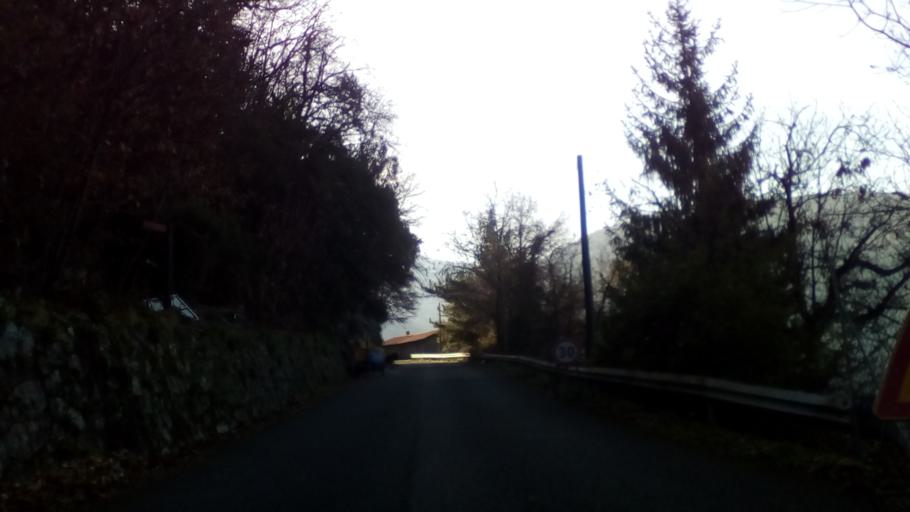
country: IT
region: Tuscany
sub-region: Provincia di Massa-Carrara
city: Montignoso
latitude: 44.0585
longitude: 10.1852
